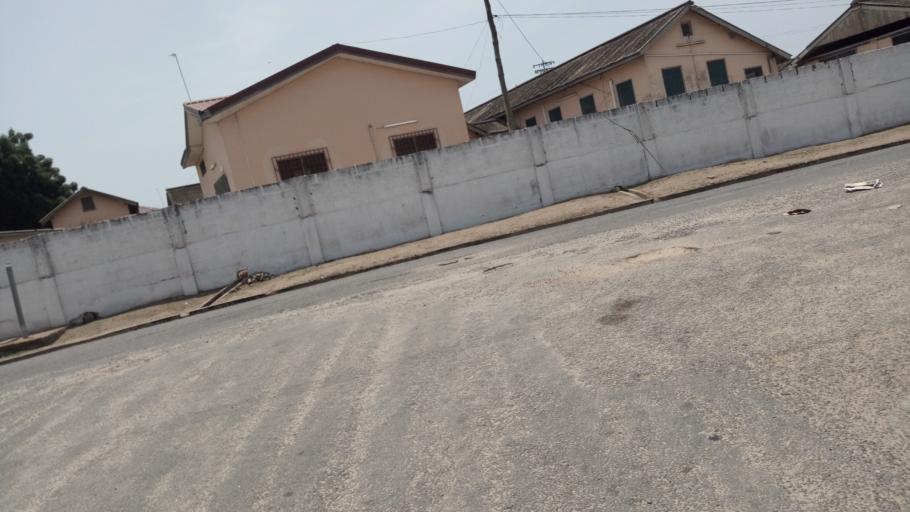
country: GH
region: Central
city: Winneba
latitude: 5.3441
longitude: -0.6232
